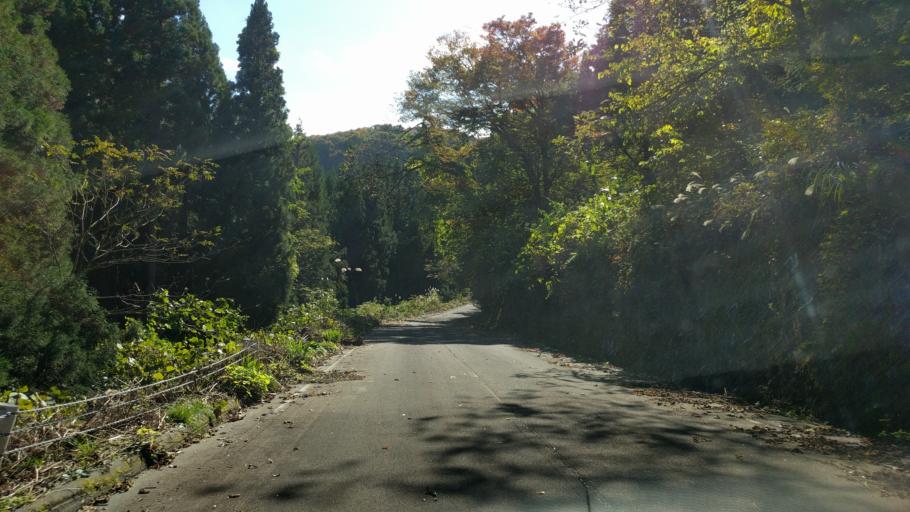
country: JP
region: Fukushima
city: Kitakata
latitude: 37.4300
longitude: 139.7812
